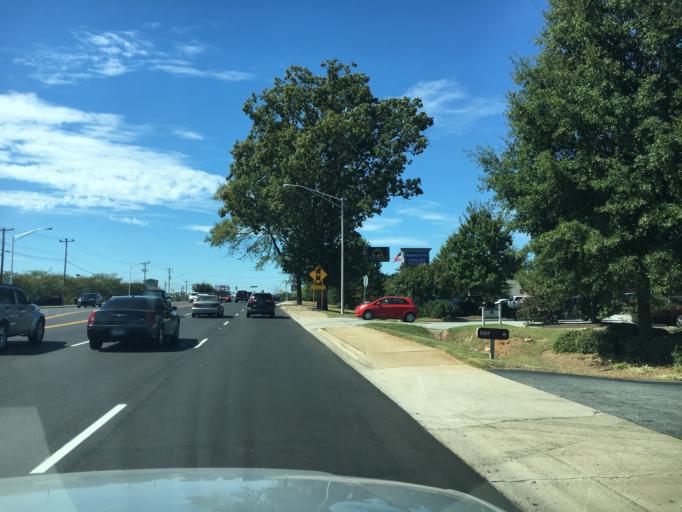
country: US
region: South Carolina
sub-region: Spartanburg County
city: Arcadia
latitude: 34.9373
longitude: -81.9839
